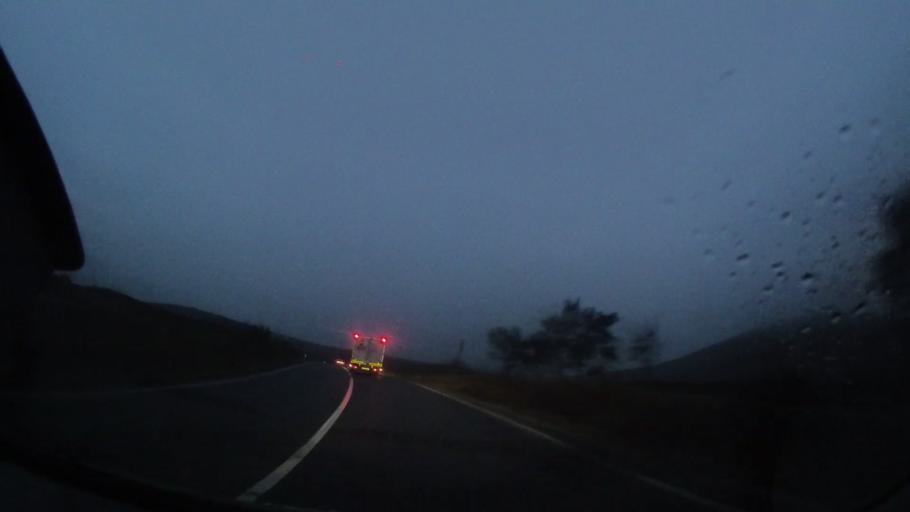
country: RO
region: Harghita
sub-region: Comuna Ditrau
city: Ditrau
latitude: 46.8376
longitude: 25.4883
